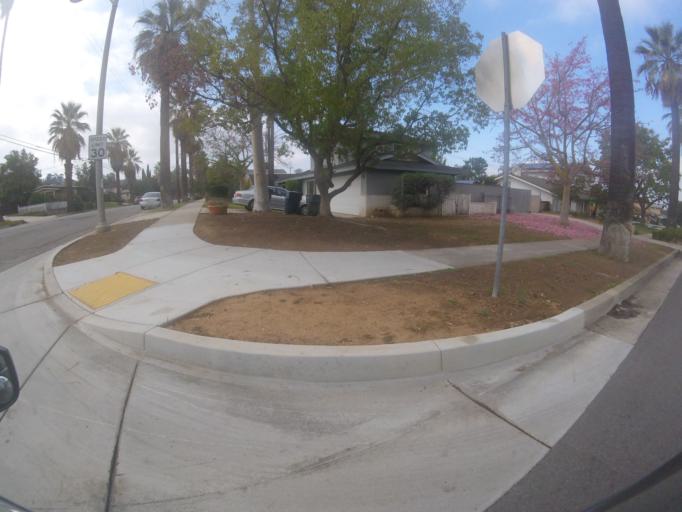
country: US
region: California
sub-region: San Bernardino County
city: Redlands
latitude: 34.0364
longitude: -117.1888
